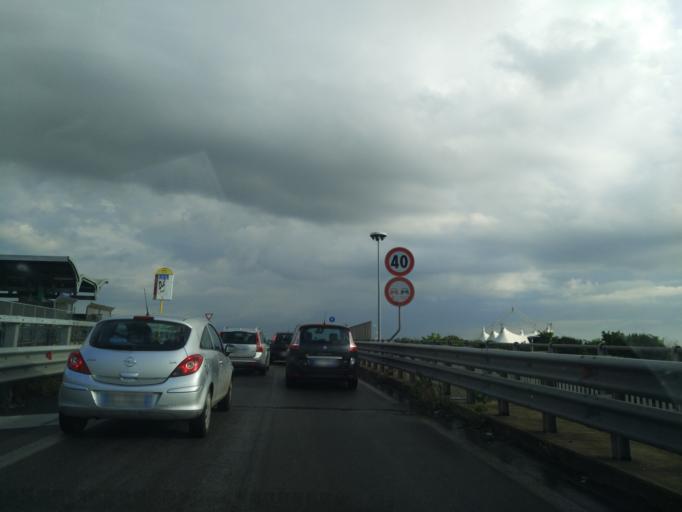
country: IT
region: Latium
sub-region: Citta metropolitana di Roma Capitale
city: Rome
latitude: 41.9037
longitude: 12.5737
